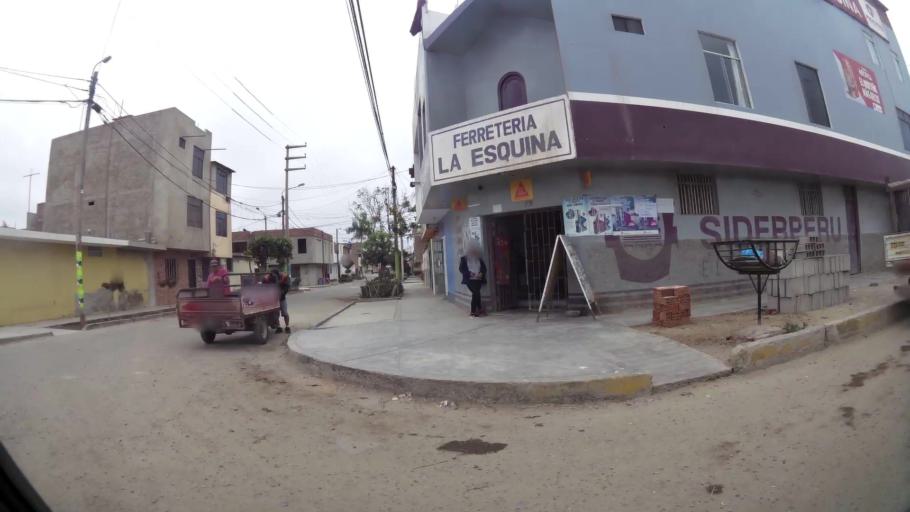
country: PE
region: La Libertad
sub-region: Provincia de Trujillo
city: Buenos Aires
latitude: -8.1448
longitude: -79.0493
